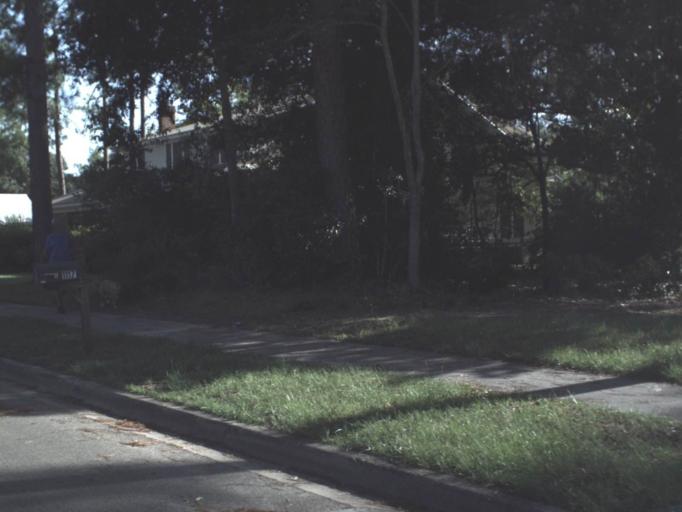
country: US
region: Florida
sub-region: Taylor County
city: Perry
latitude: 30.1259
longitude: -83.5821
